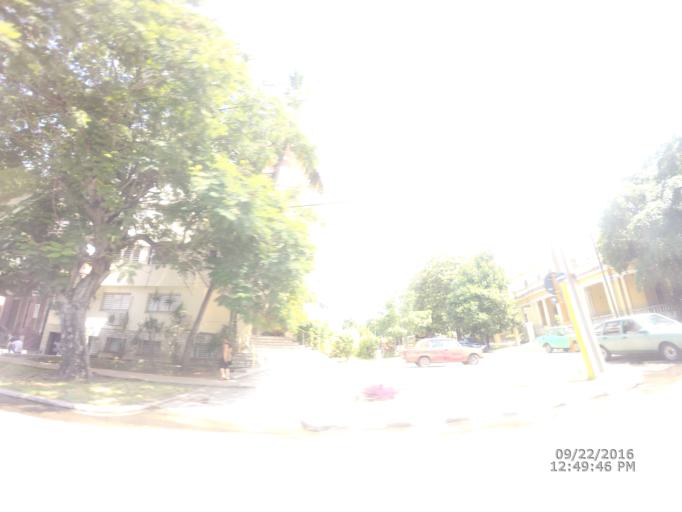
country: CU
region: La Habana
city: Havana
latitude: 23.1350
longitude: -82.3974
